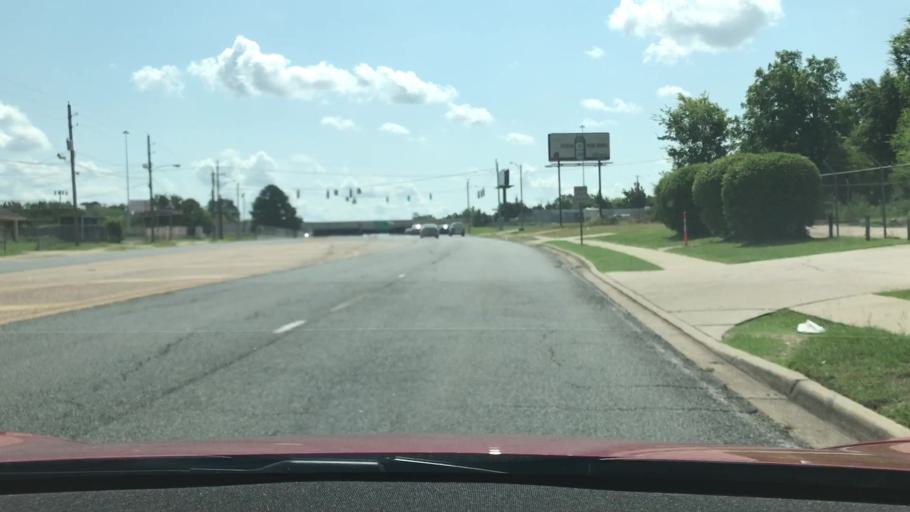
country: US
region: Louisiana
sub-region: Bossier Parish
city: Bossier City
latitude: 32.4419
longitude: -93.7602
